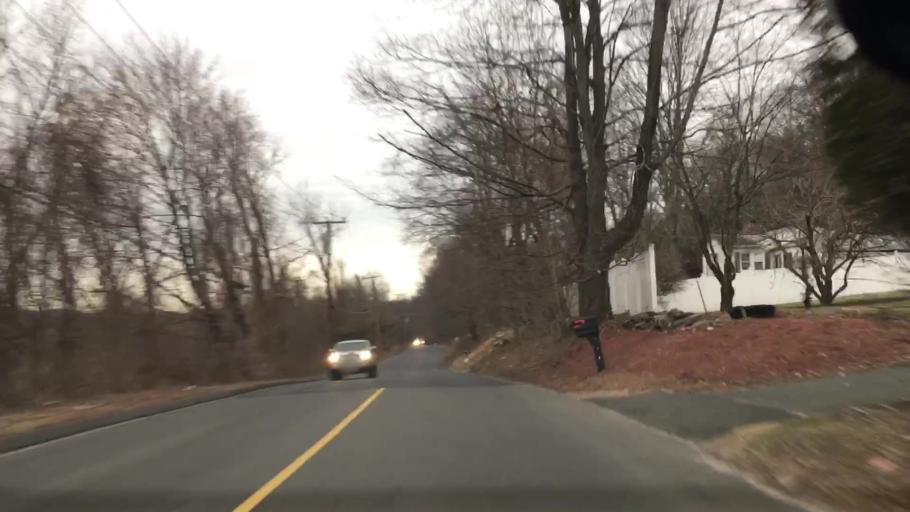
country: US
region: Connecticut
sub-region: Fairfield County
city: Bethel
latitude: 41.4098
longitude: -73.4036
